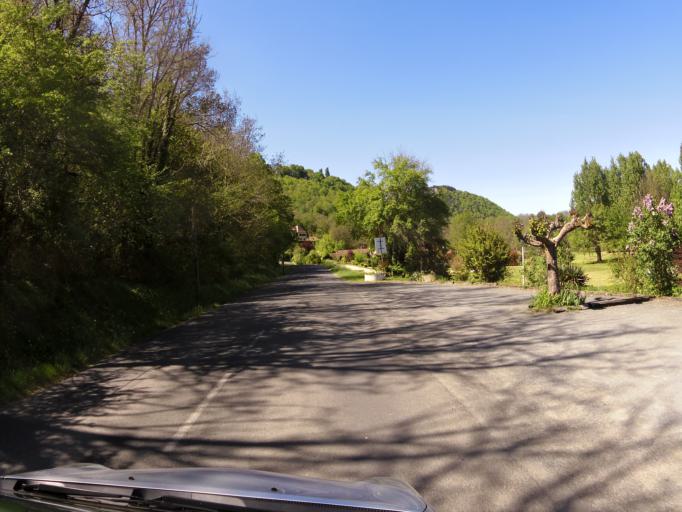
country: FR
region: Aquitaine
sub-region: Departement de la Dordogne
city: Cenac-et-Saint-Julien
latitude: 44.7893
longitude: 1.1642
